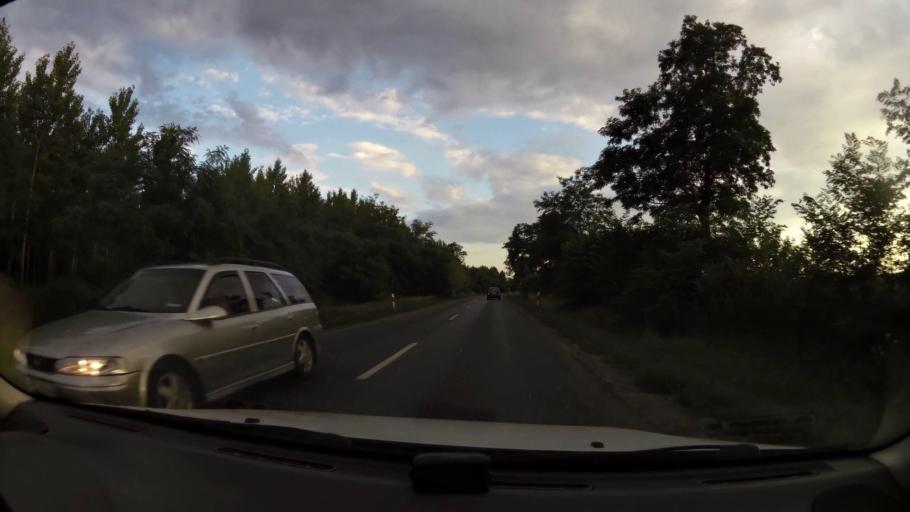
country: HU
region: Pest
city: Tapioszele
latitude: 47.3142
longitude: 19.8739
